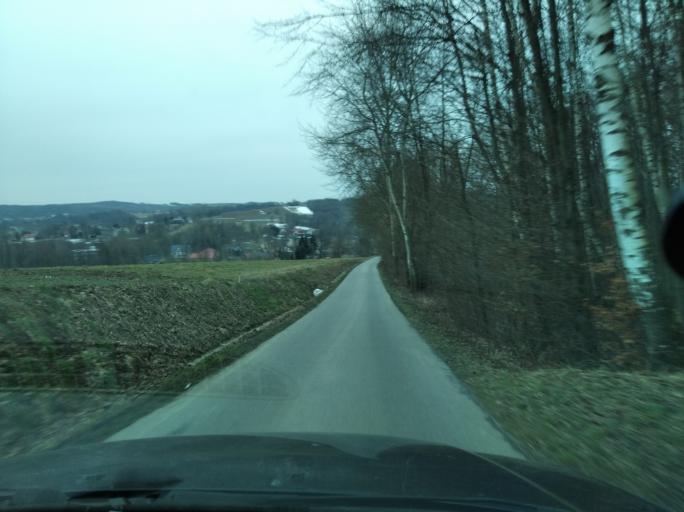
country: PL
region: Subcarpathian Voivodeship
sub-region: Powiat rzeszowski
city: Chmielnik
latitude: 49.9809
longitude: 22.1350
